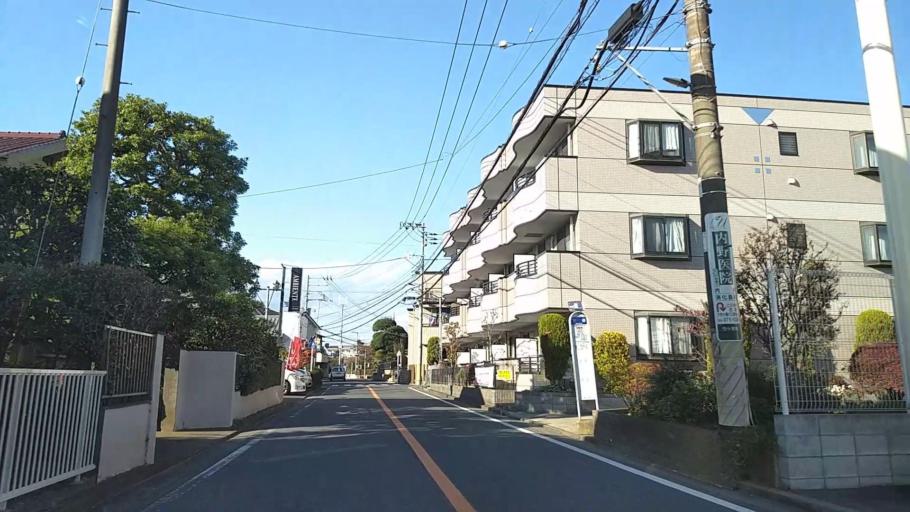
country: JP
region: Tokyo
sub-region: Machida-shi
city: Machida
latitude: 35.5405
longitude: 139.5434
